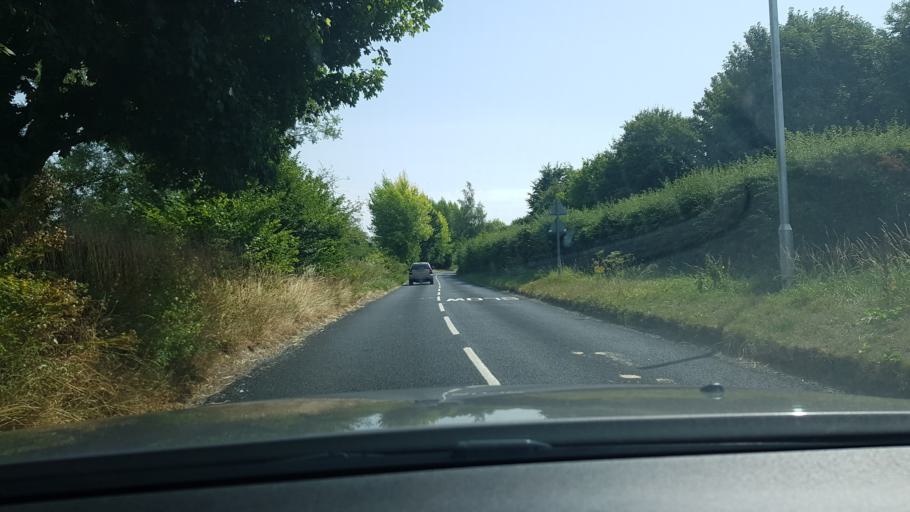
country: GB
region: England
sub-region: West Berkshire
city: Lambourn
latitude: 51.4910
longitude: -1.4976
